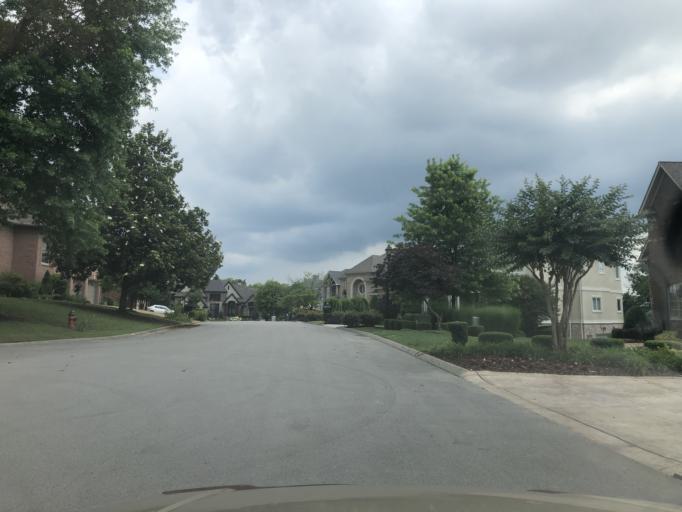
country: US
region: Tennessee
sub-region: Davidson County
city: Lakewood
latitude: 36.2398
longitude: -86.6031
